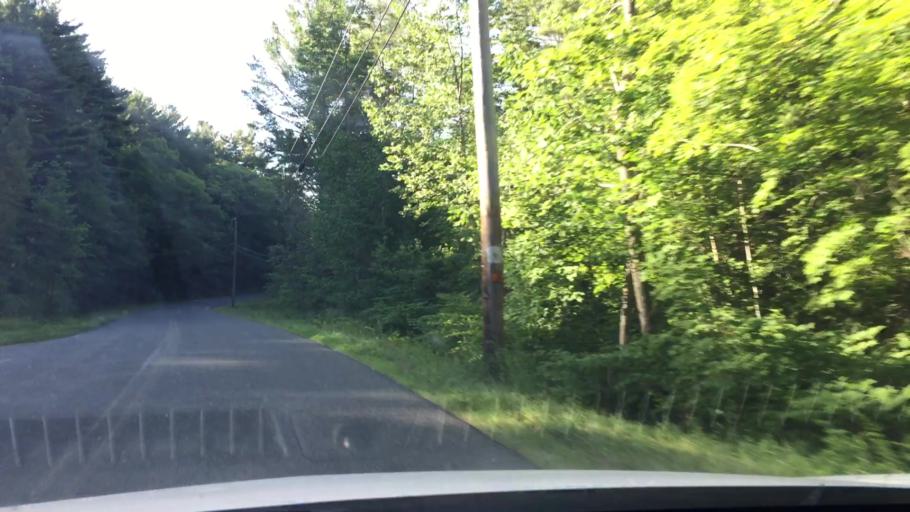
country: US
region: Massachusetts
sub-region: Berkshire County
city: Lee
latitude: 42.2789
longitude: -73.2092
